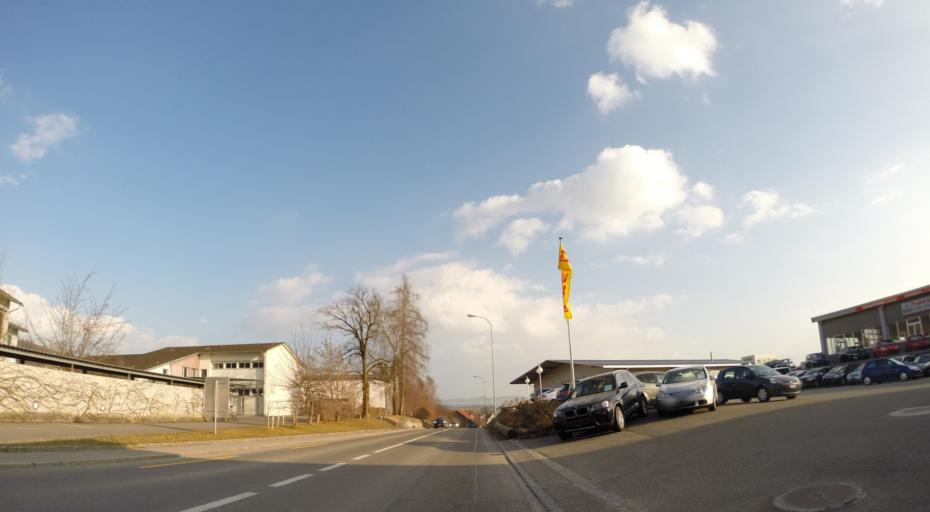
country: CH
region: Thurgau
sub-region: Frauenfeld District
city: Huttwilen
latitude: 47.6099
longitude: 8.8671
